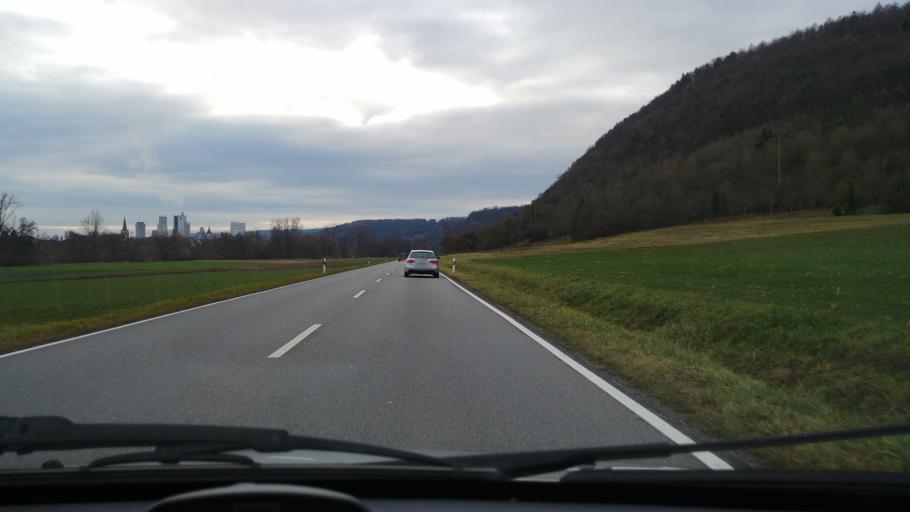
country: DE
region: Bavaria
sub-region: Regierungsbezirk Unterfranken
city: Karlstadt
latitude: 49.9709
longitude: 9.7590
